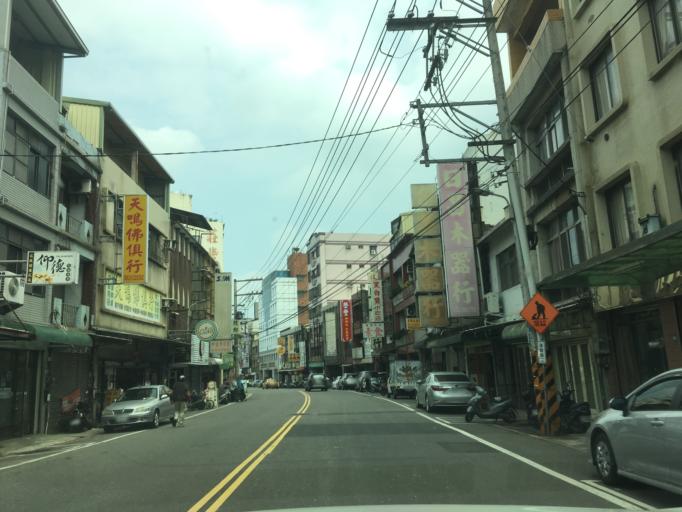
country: TW
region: Taiwan
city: Daxi
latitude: 24.8784
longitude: 121.2882
